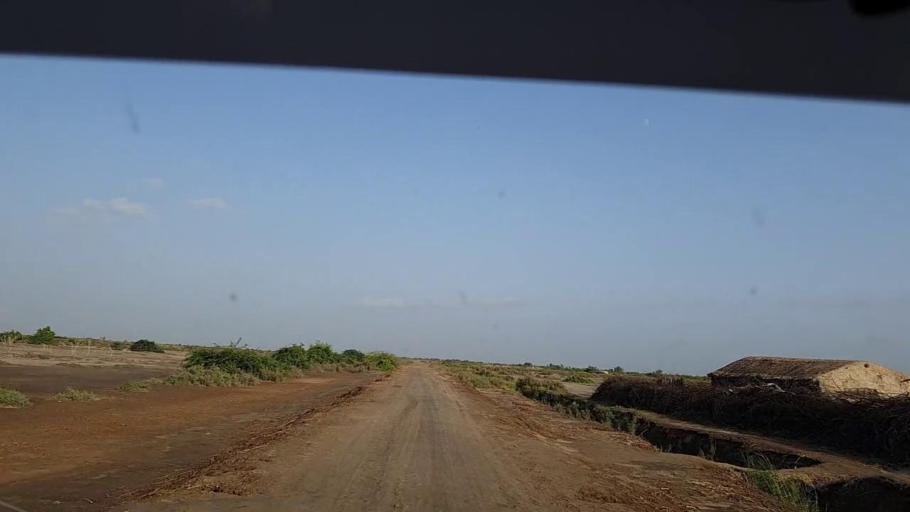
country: PK
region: Sindh
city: Badin
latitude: 24.5517
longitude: 68.8724
